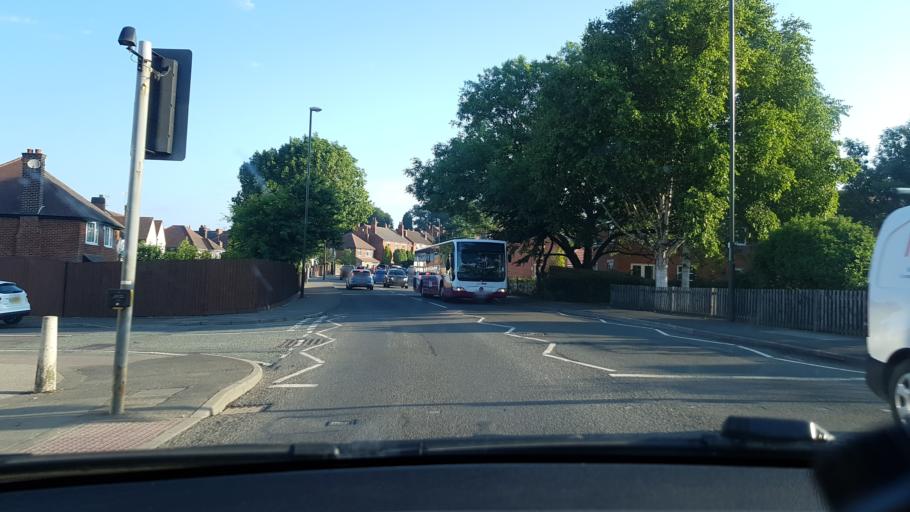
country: GB
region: England
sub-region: Derbyshire
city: Ilkeston
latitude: 52.9620
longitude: -1.3074
